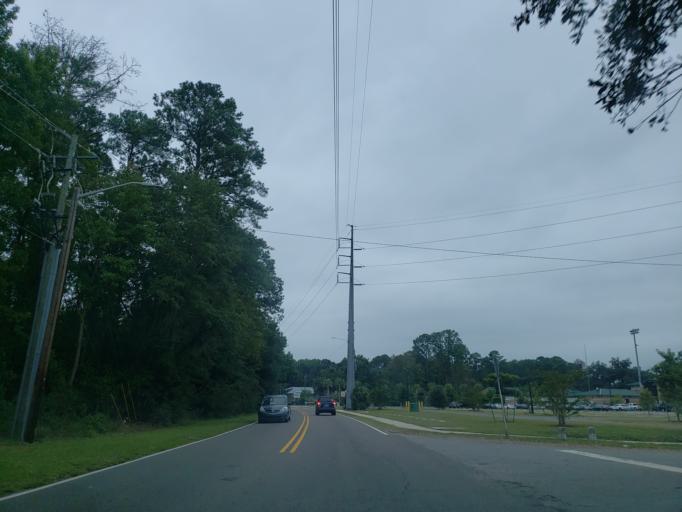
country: US
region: Georgia
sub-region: Chatham County
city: Isle of Hope
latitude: 31.9948
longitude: -81.0784
